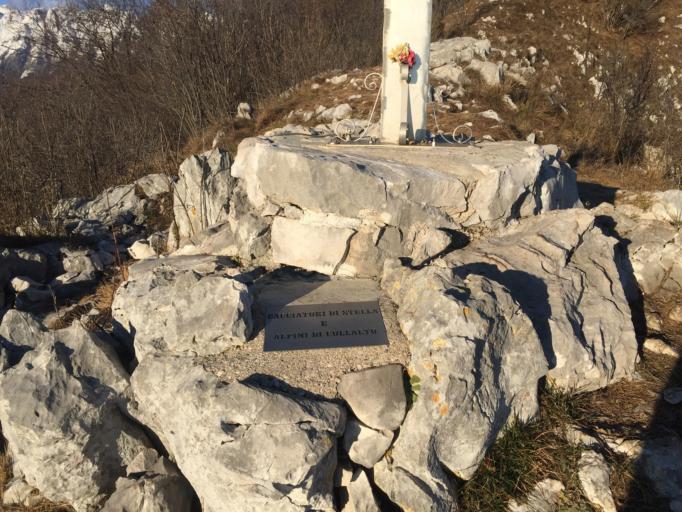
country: IT
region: Friuli Venezia Giulia
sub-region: Provincia di Udine
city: Tarcento
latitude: 46.2451
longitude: 13.2332
